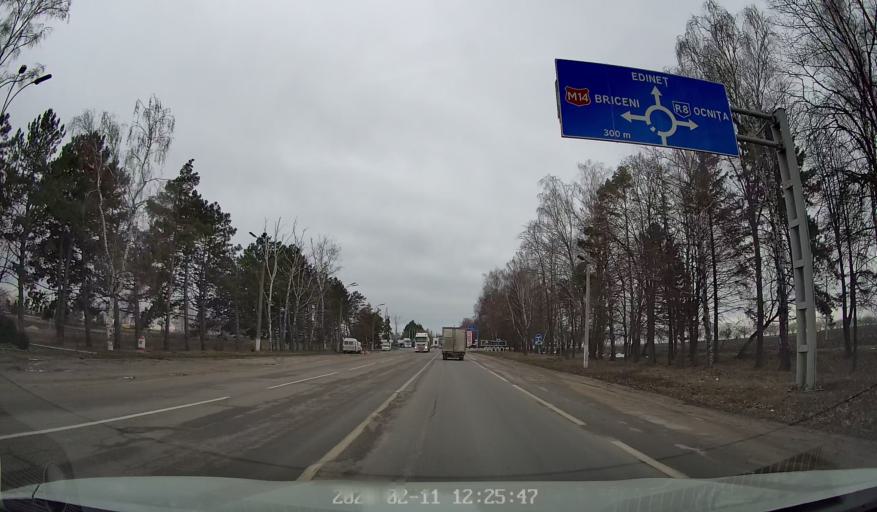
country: MD
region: Raionul Edinet
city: Edinet
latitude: 48.1572
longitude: 27.3327
